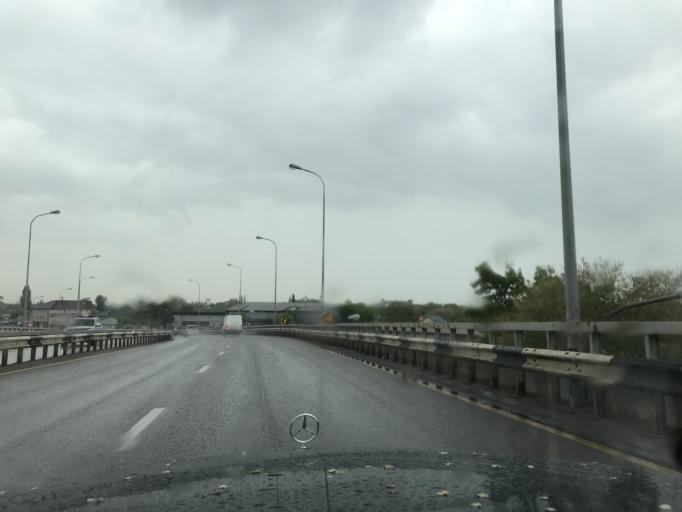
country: KZ
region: Almaty Oblysy
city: Pervomayskiy
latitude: 43.3380
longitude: 76.9647
